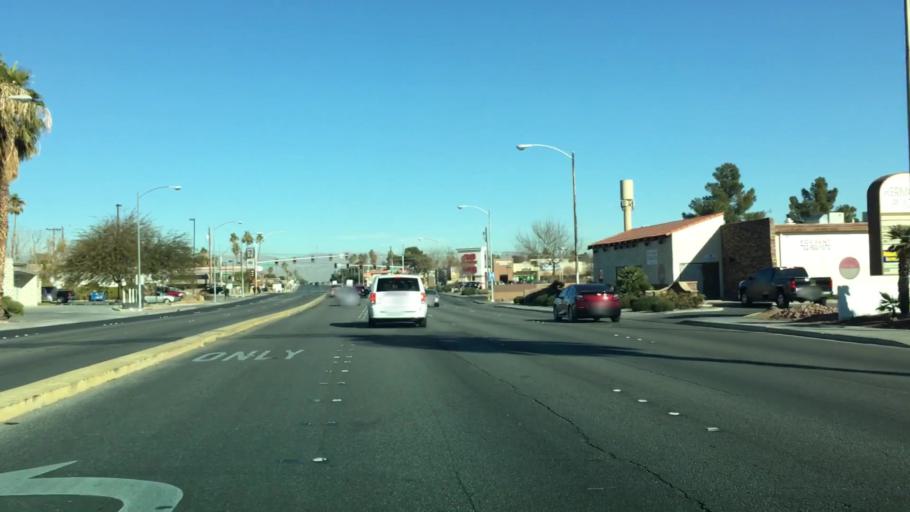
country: US
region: Nevada
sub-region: Clark County
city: Winchester
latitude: 36.1281
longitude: -115.1186
